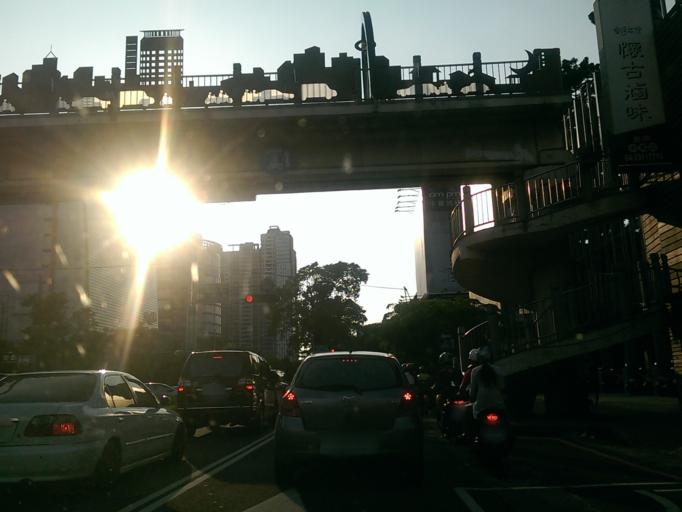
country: TW
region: Taiwan
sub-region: Taichung City
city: Taichung
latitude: 24.1644
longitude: 120.6470
